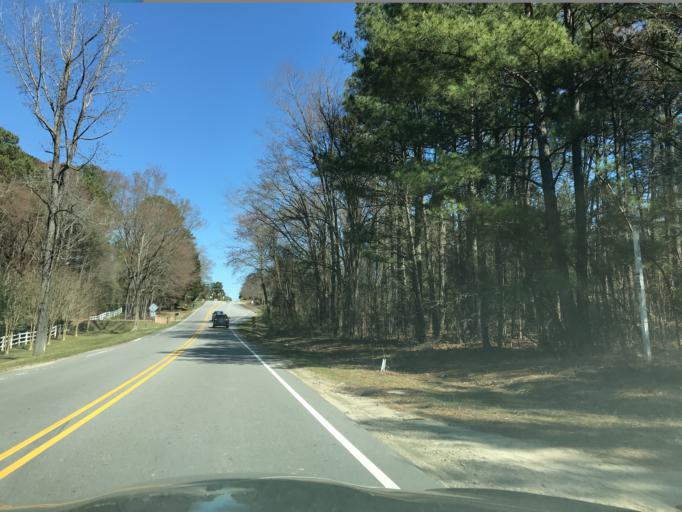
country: US
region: North Carolina
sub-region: Wake County
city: Wake Forest
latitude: 35.9472
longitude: -78.5748
